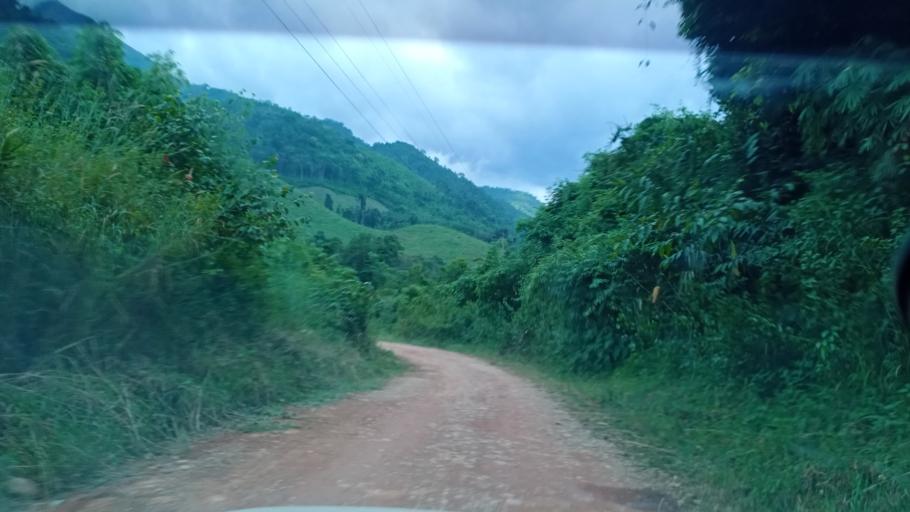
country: TH
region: Changwat Bueng Kan
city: Pak Khat
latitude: 18.7248
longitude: 103.2421
